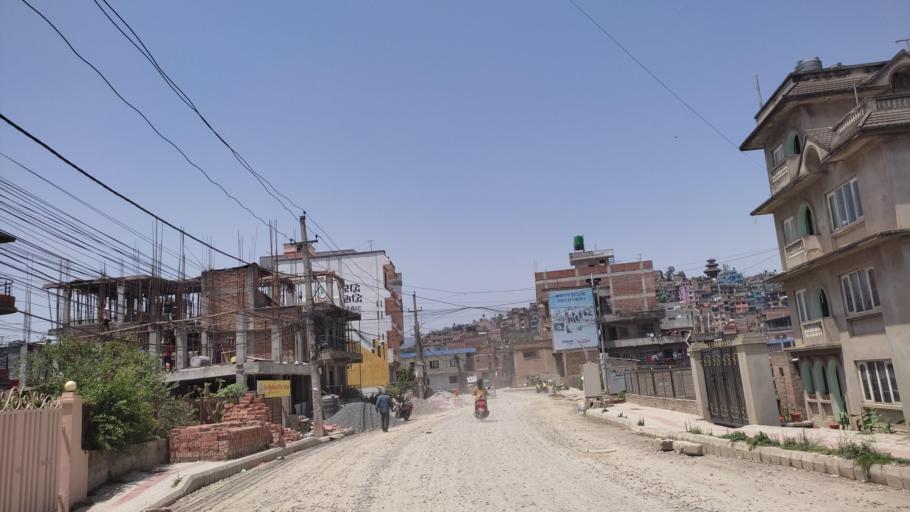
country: NP
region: Central Region
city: Kirtipur
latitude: 27.6763
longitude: 85.2728
